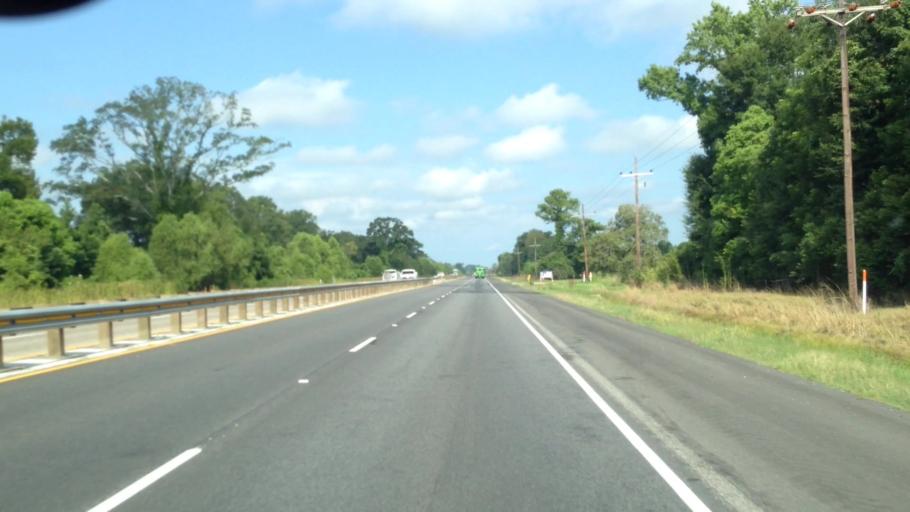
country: US
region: Louisiana
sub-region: Pointe Coupee Parish
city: Livonia
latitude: 30.5558
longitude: -91.6027
